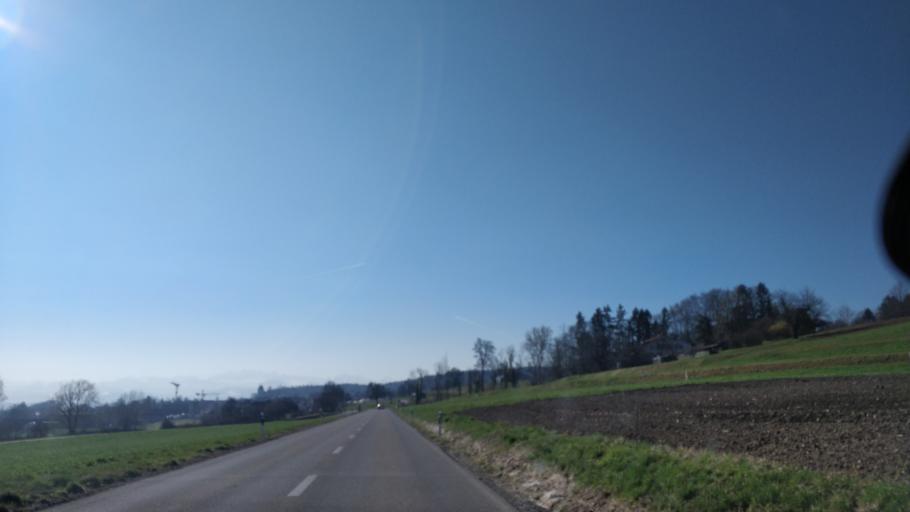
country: CH
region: Zurich
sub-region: Bezirk Uster
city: Aesch
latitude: 47.3471
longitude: 8.6640
